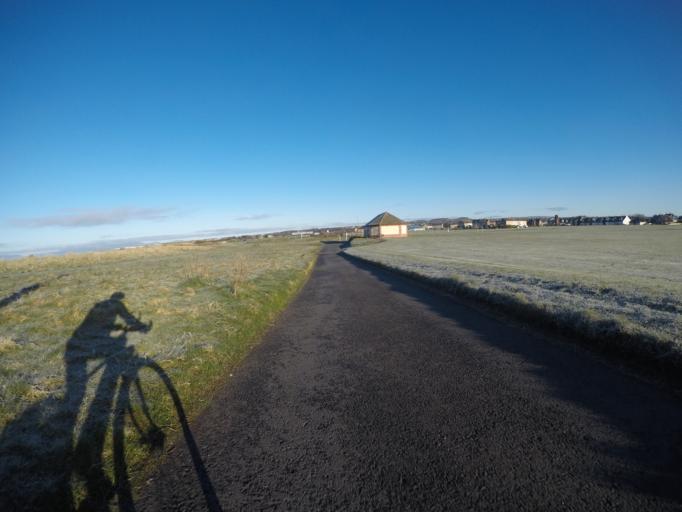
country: GB
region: Scotland
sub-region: North Ayrshire
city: Stevenston
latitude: 55.6295
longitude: -4.7503
